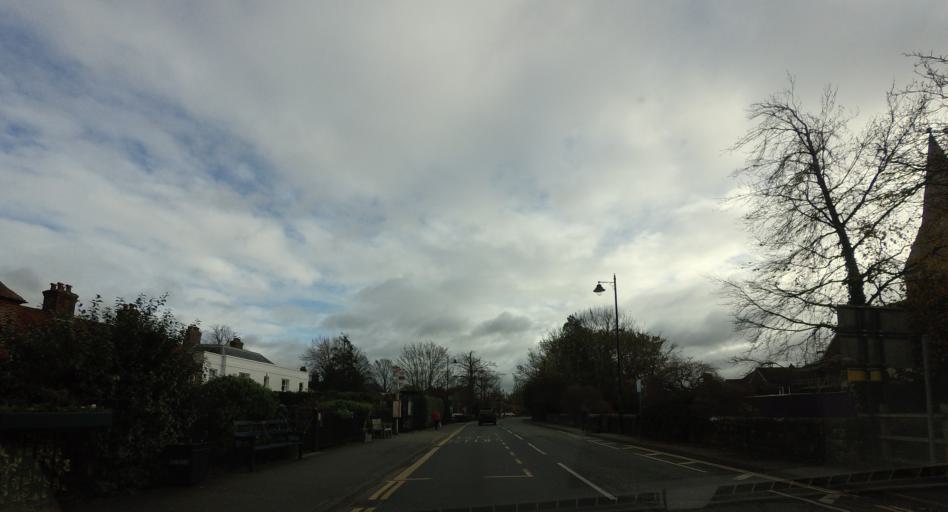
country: GB
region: England
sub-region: Kent
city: Hawkhurst
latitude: 51.0473
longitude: 0.5122
